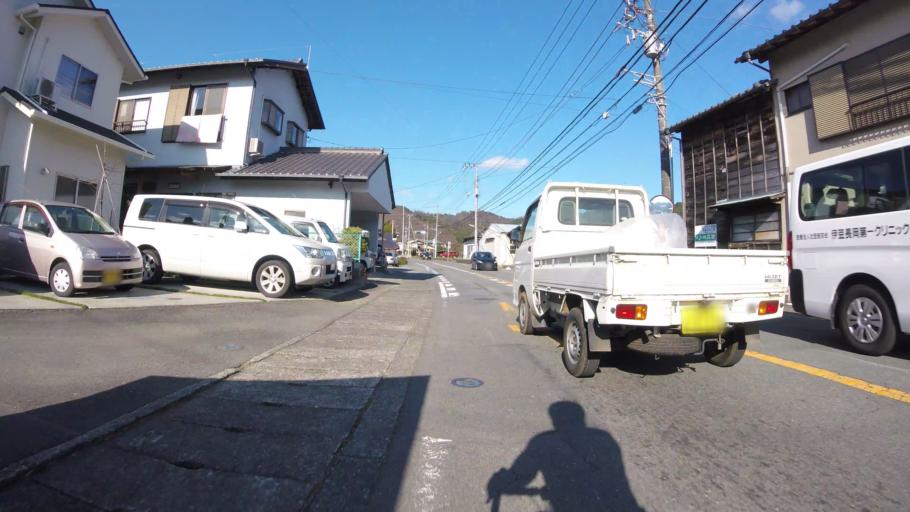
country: JP
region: Shizuoka
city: Ito
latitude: 34.9884
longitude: 138.9536
